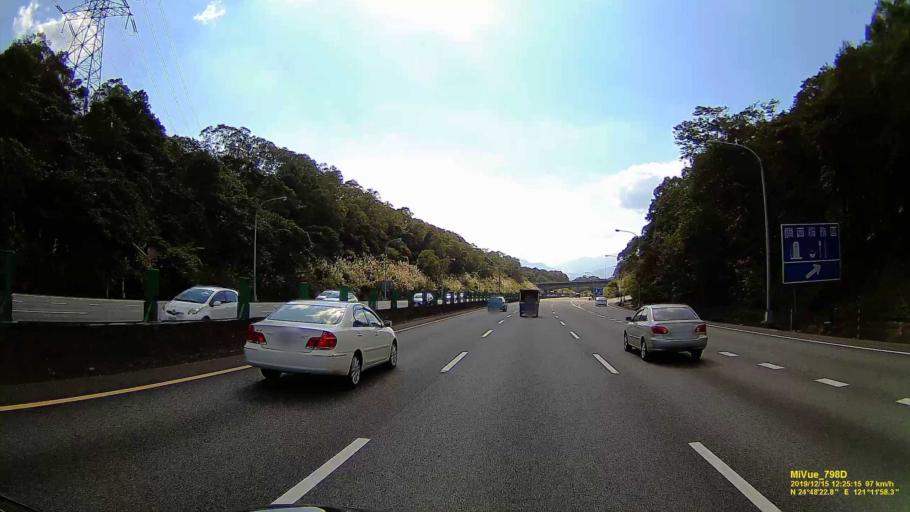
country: TW
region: Taiwan
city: Daxi
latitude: 24.8058
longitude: 121.1993
